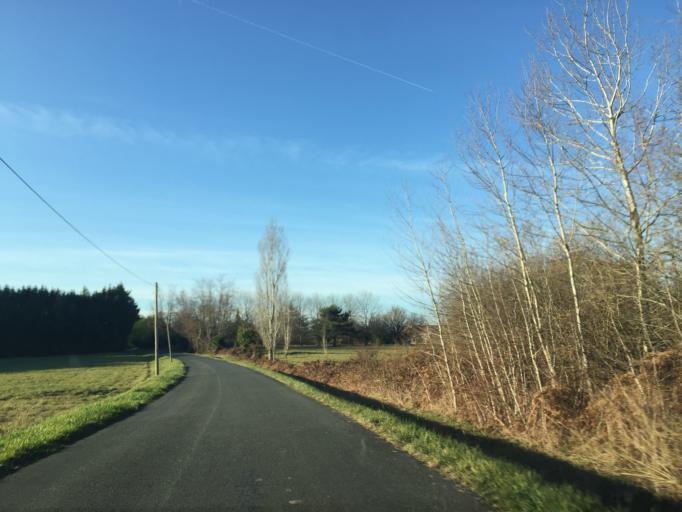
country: FR
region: Aquitaine
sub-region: Departement de la Dordogne
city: Riberac
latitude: 45.2049
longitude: 0.3157
